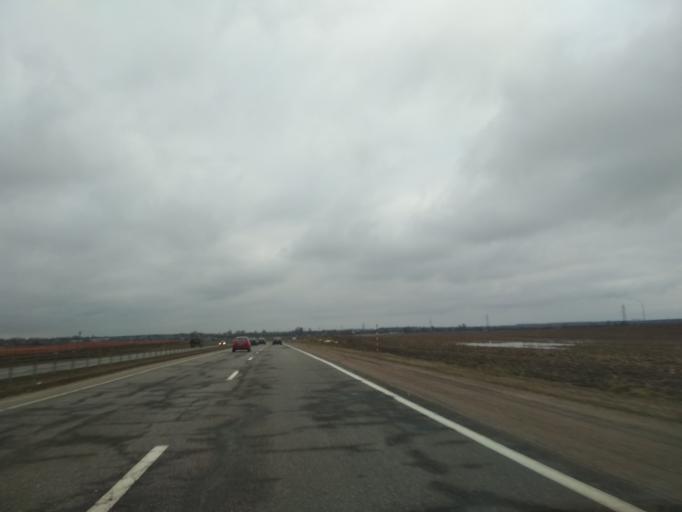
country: BY
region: Minsk
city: Dukora
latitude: 53.6805
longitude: 27.9221
